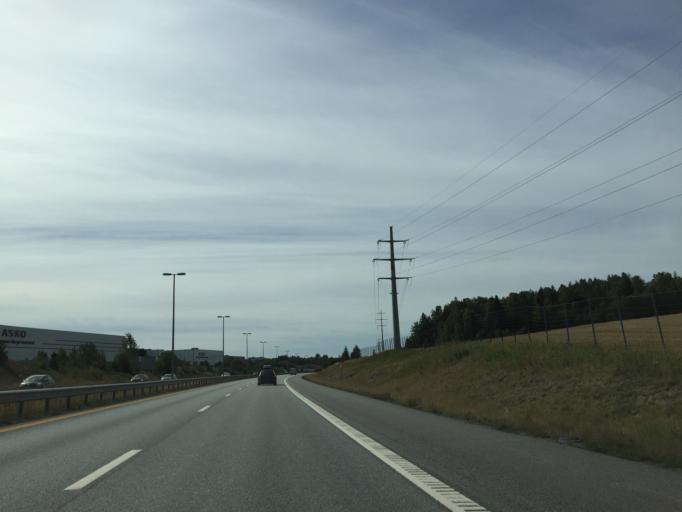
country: NO
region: Akershus
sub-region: Vestby
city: Vestby
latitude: 59.5945
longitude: 10.7388
